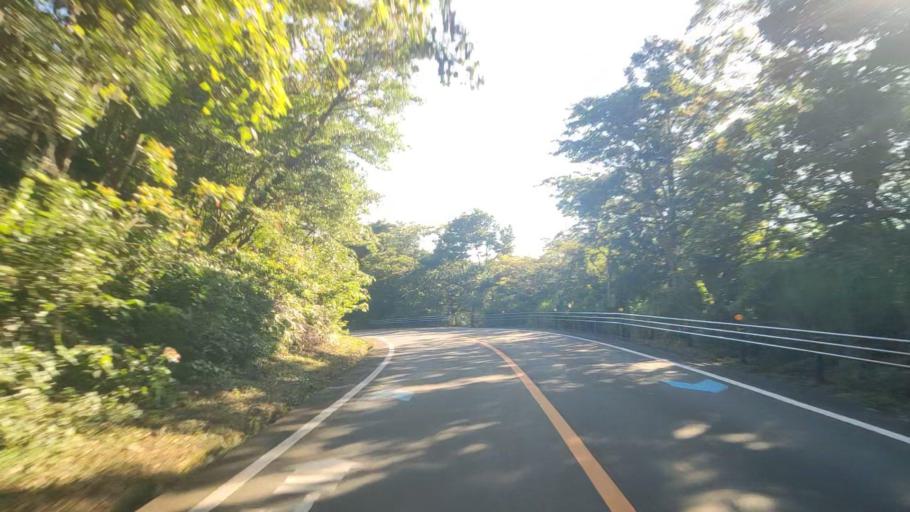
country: JP
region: Mie
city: Toba
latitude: 34.4080
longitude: 136.8908
